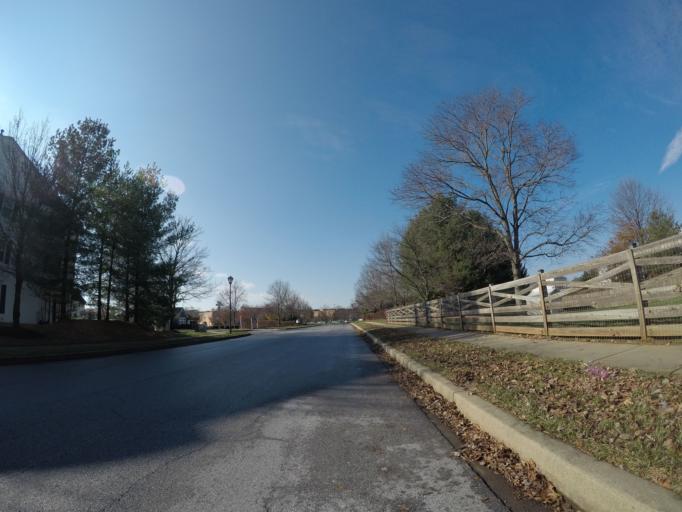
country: US
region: Maryland
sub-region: Frederick County
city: Ballenger Creek
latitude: 39.3711
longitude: -77.4411
